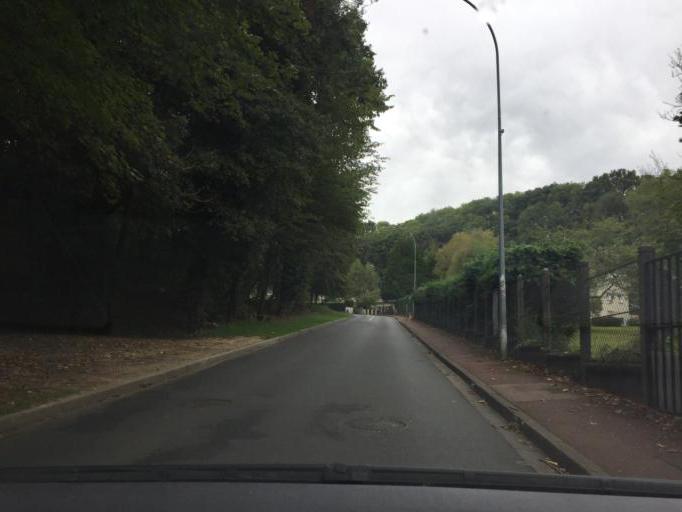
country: FR
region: Ile-de-France
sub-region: Departement de l'Essonne
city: Villiers-le-Bacle
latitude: 48.7241
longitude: 2.1238
